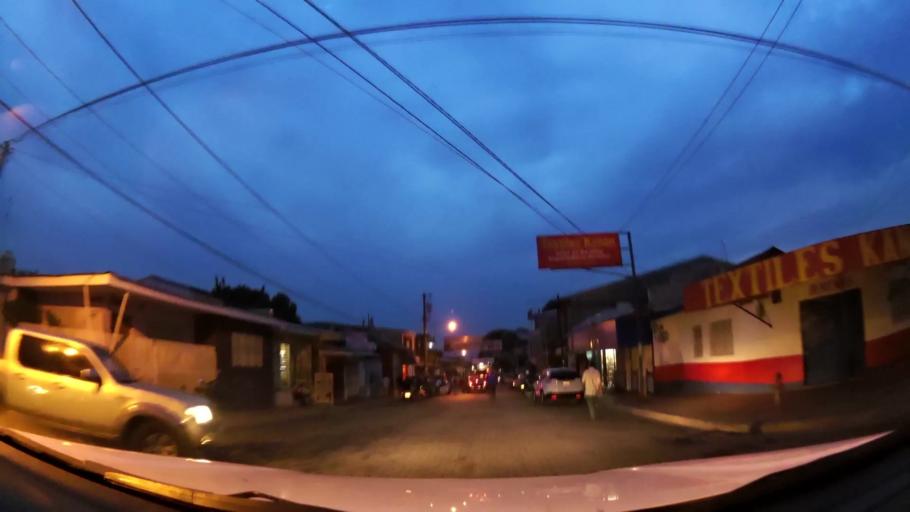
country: NI
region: Esteli
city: Esteli
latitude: 13.0836
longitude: -86.3563
